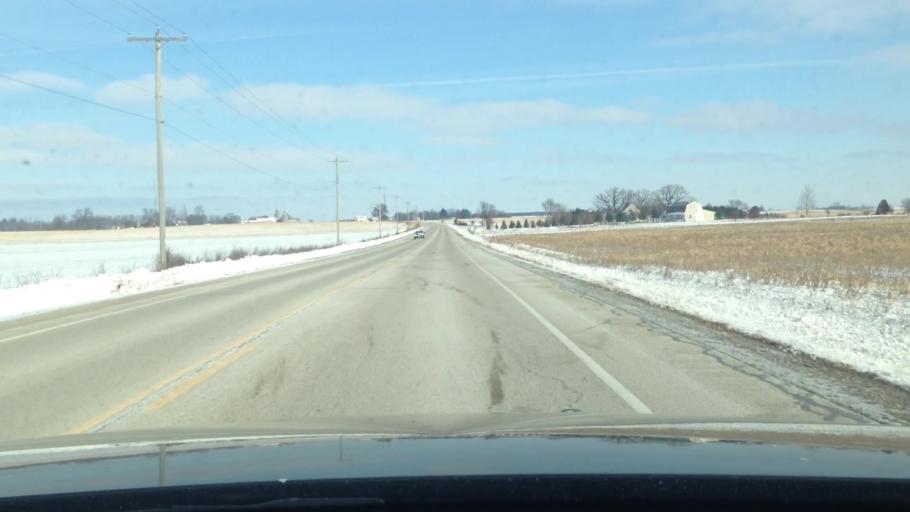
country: US
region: Wisconsin
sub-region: Walworth County
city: Lake Geneva
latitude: 42.6775
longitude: -88.4078
